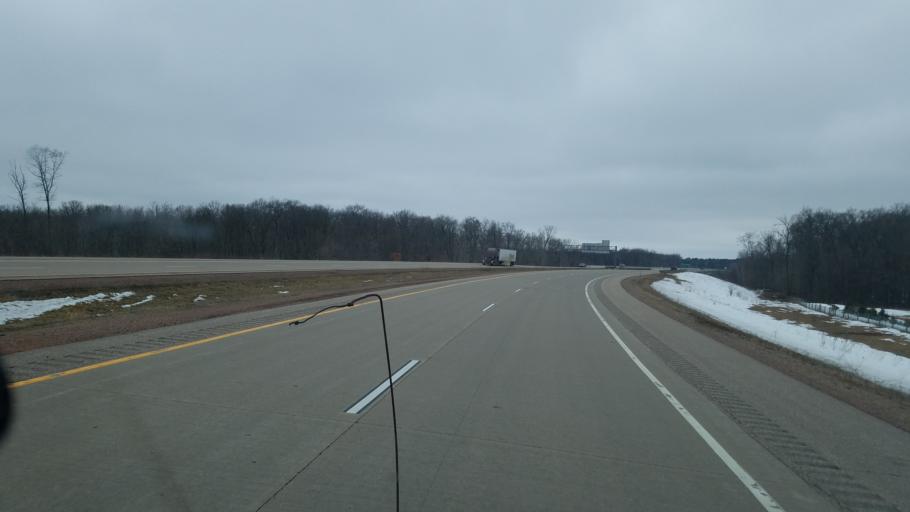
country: US
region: Wisconsin
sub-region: Portage County
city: Stevens Point
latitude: 44.5960
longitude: -89.6352
